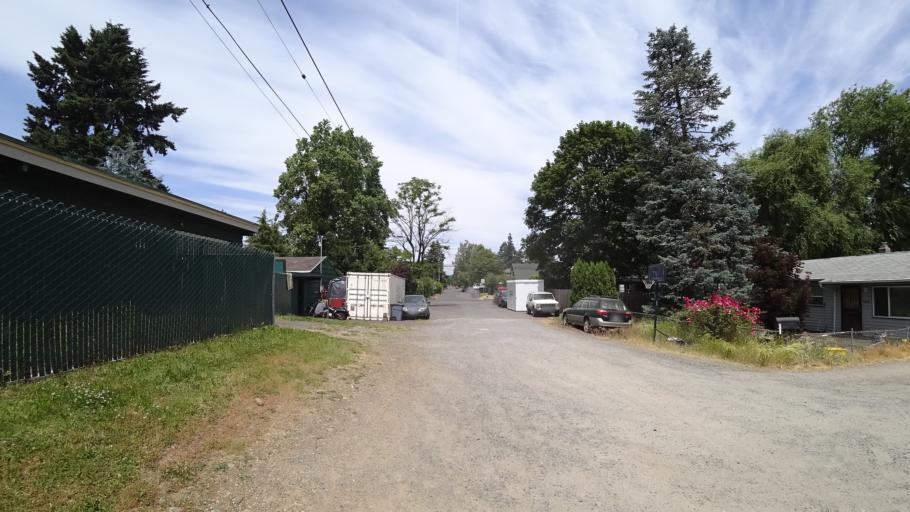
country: US
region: Oregon
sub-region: Multnomah County
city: Lents
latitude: 45.4681
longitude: -122.5943
